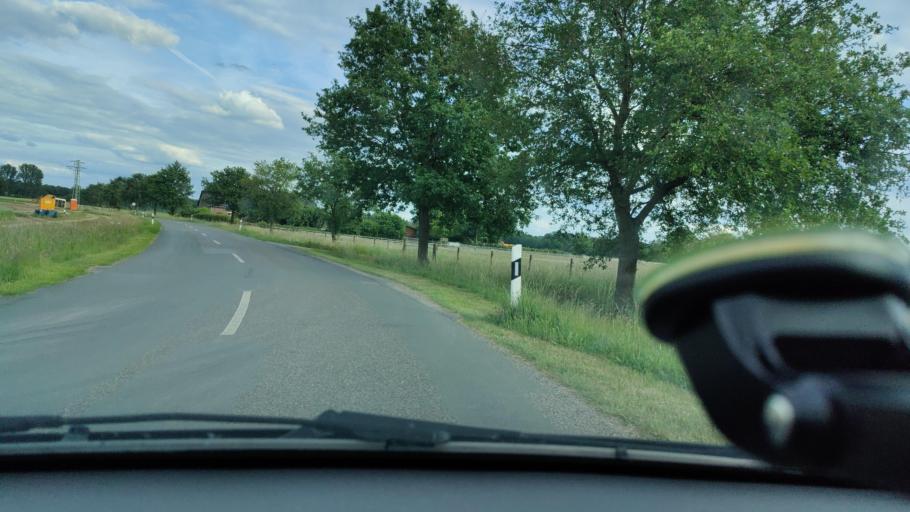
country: DE
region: North Rhine-Westphalia
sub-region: Regierungsbezirk Dusseldorf
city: Weeze
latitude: 51.6281
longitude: 6.1584
